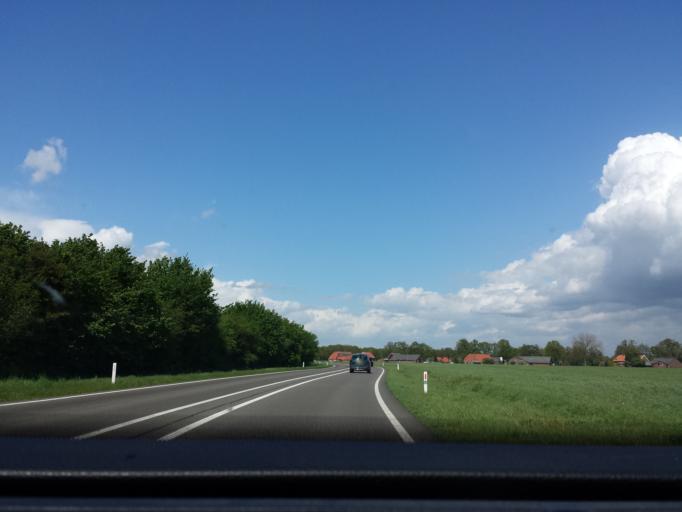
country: NL
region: Gelderland
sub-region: Gemeente Lochem
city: Barchem
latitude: 52.0813
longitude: 6.4640
